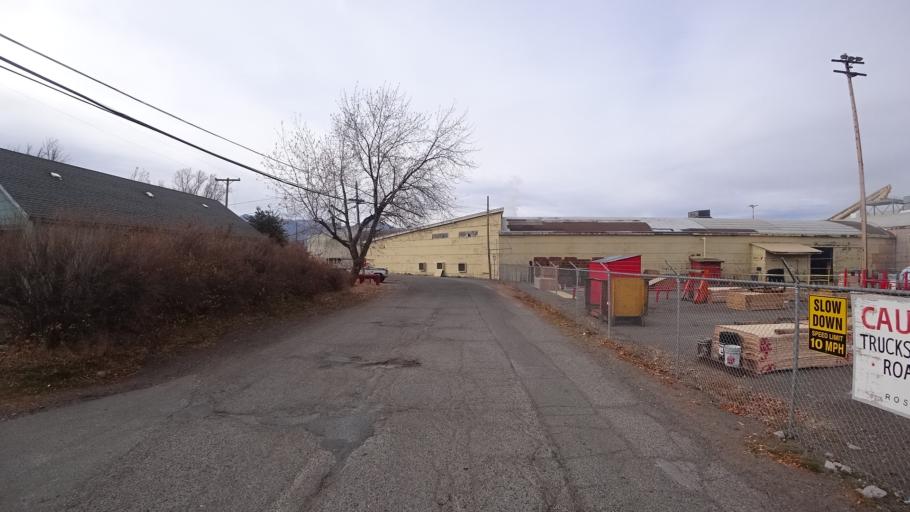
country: US
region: California
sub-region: Siskiyou County
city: Weed
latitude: 41.4333
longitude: -122.3778
